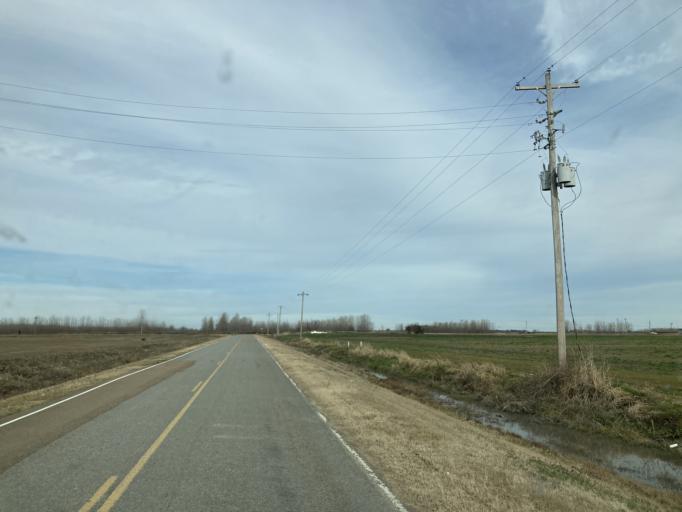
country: US
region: Mississippi
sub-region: Humphreys County
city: Belzoni
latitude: 33.1808
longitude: -90.6065
